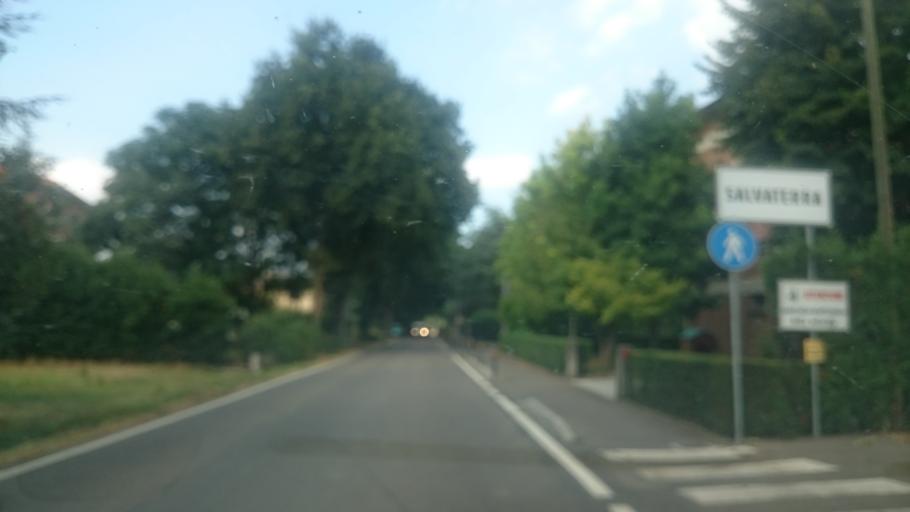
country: IT
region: Emilia-Romagna
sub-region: Provincia di Reggio Emilia
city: Salvaterra
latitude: 44.5948
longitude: 10.7609
